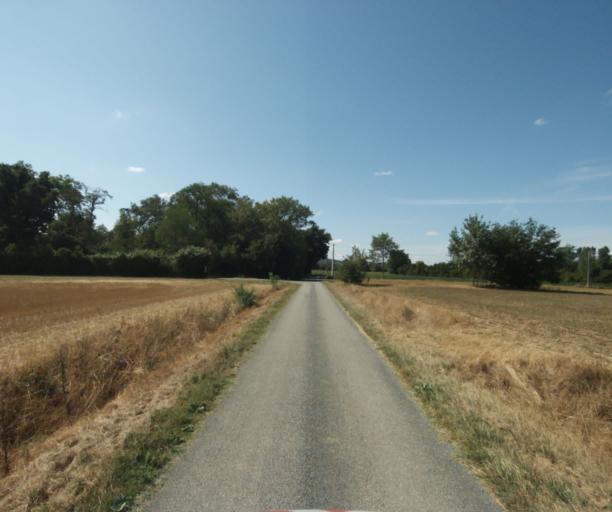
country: FR
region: Midi-Pyrenees
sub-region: Departement de la Haute-Garonne
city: Revel
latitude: 43.4896
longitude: 1.9700
